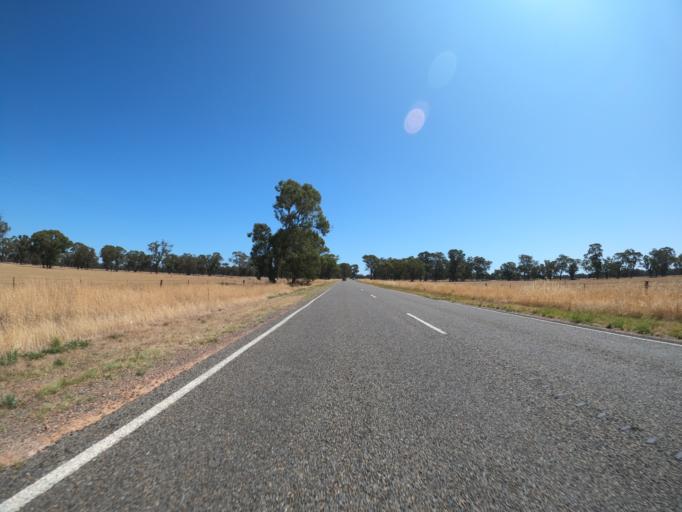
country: AU
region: New South Wales
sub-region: Corowa Shire
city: Corowa
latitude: -36.0821
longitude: 146.3364
